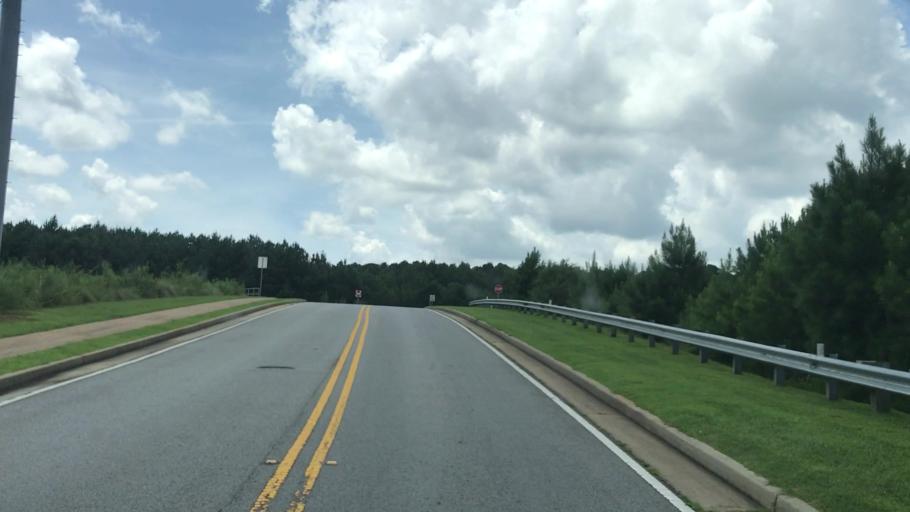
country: US
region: Georgia
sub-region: Gwinnett County
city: Suwanee
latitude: 34.0248
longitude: -84.0525
